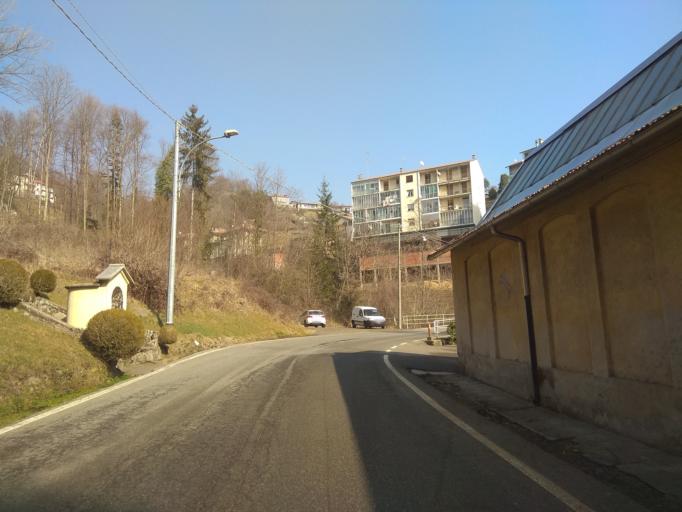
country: IT
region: Piedmont
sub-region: Provincia di Biella
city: Mosso Santa Maria
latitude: 45.6481
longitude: 8.1335
